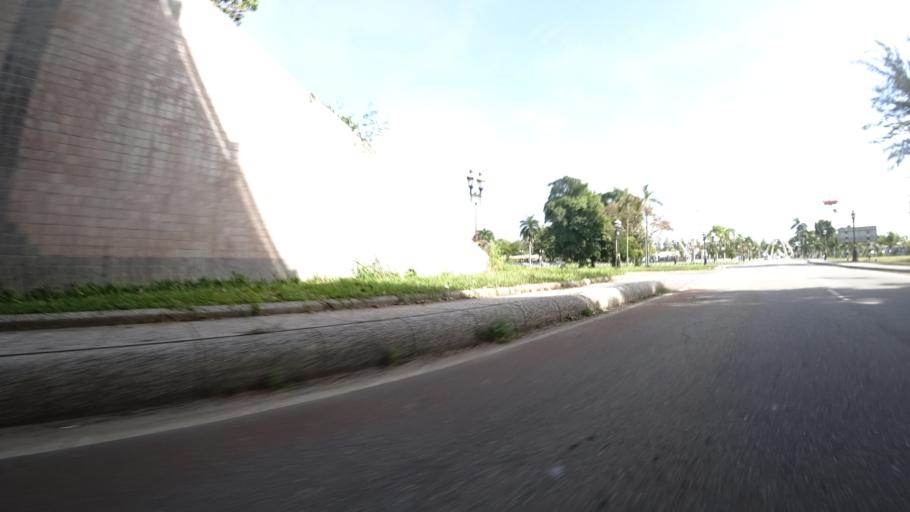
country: BN
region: Brunei and Muara
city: Bandar Seri Begawan
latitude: 4.9396
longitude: 114.8340
